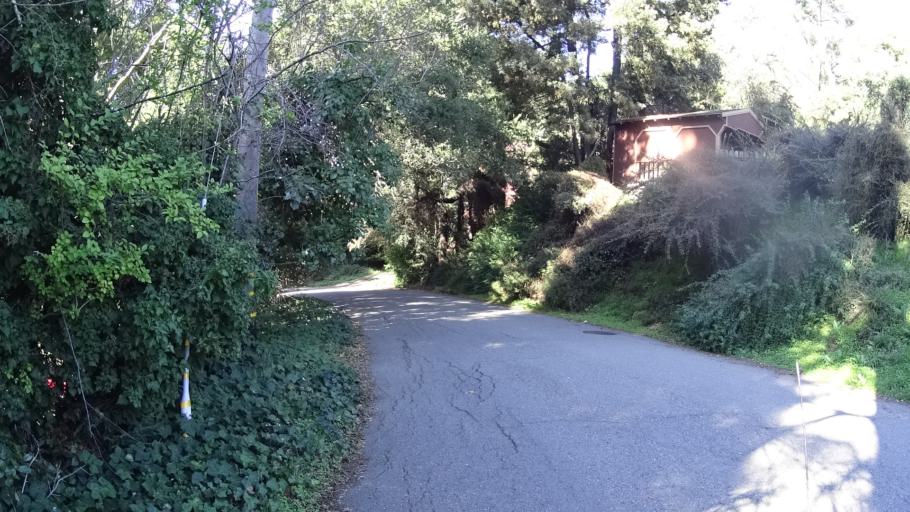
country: US
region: California
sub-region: Alameda County
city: Piedmont
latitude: 37.8387
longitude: -122.2138
